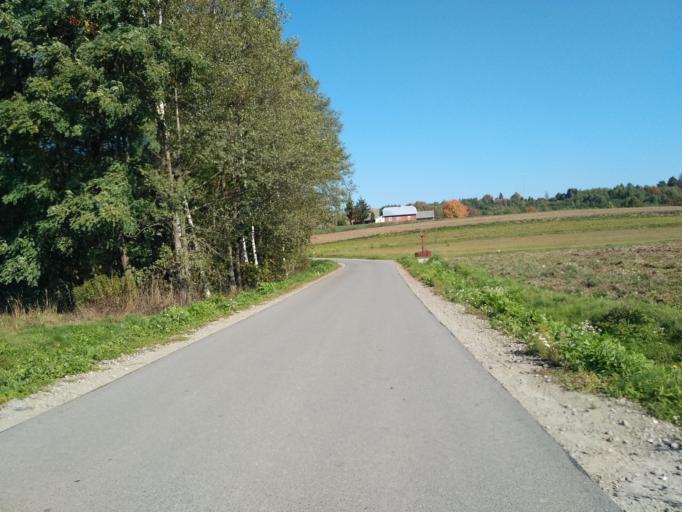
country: PL
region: Subcarpathian Voivodeship
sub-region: Powiat debicki
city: Brzostek
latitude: 49.9529
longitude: 21.3864
